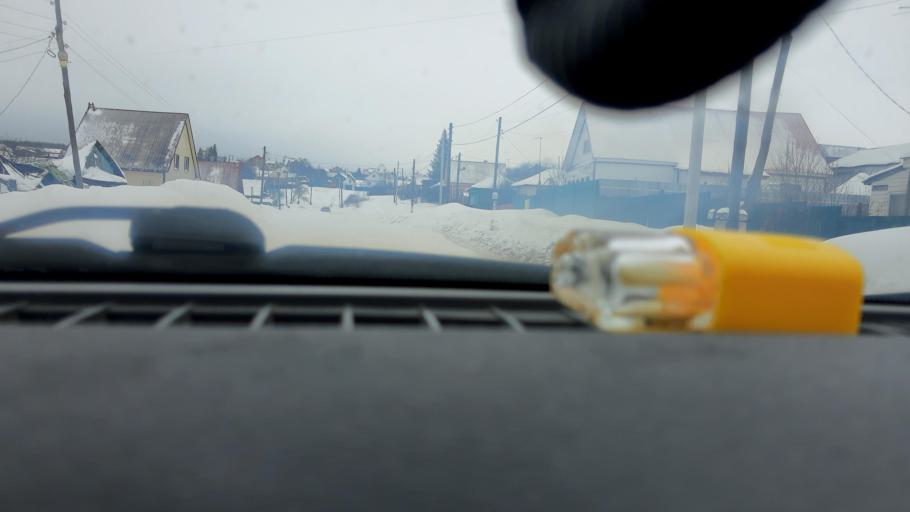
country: RU
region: Bashkortostan
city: Iglino
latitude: 54.8386
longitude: 56.4137
